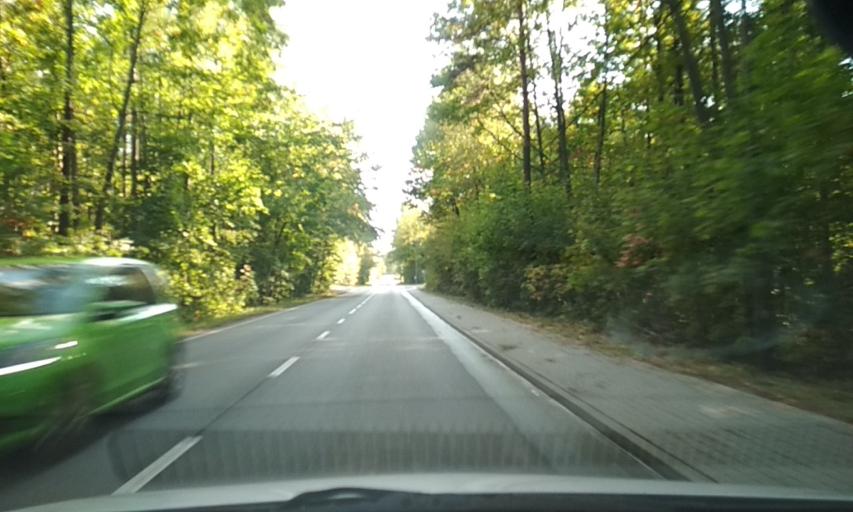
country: PL
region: Silesian Voivodeship
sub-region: Myslowice
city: Myslowice
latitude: 50.1717
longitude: 19.1571
